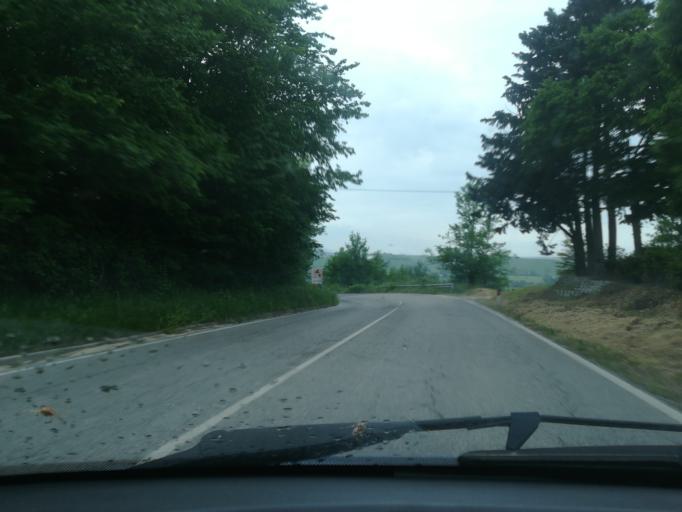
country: IT
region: The Marches
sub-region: Provincia di Macerata
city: Casette Verdini
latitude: 43.2869
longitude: 13.3918
